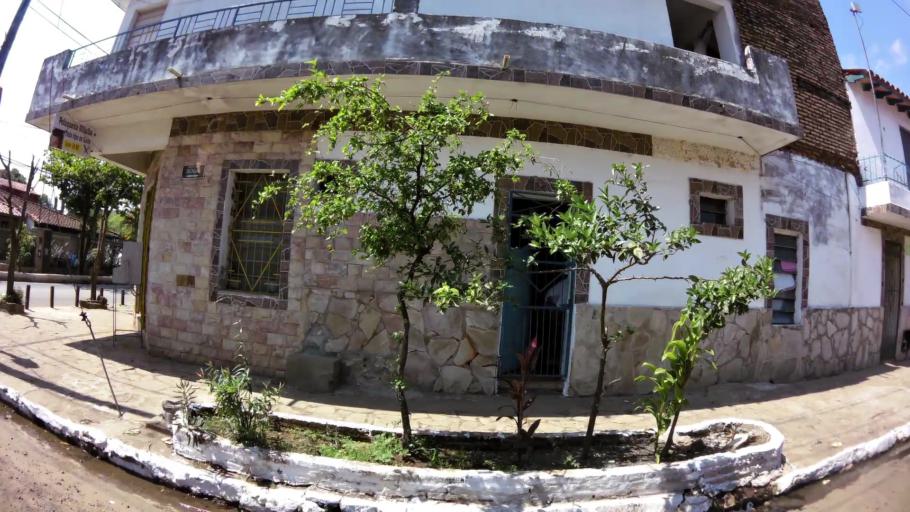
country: PY
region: Central
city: Fernando de la Mora
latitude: -25.3272
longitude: -57.5609
